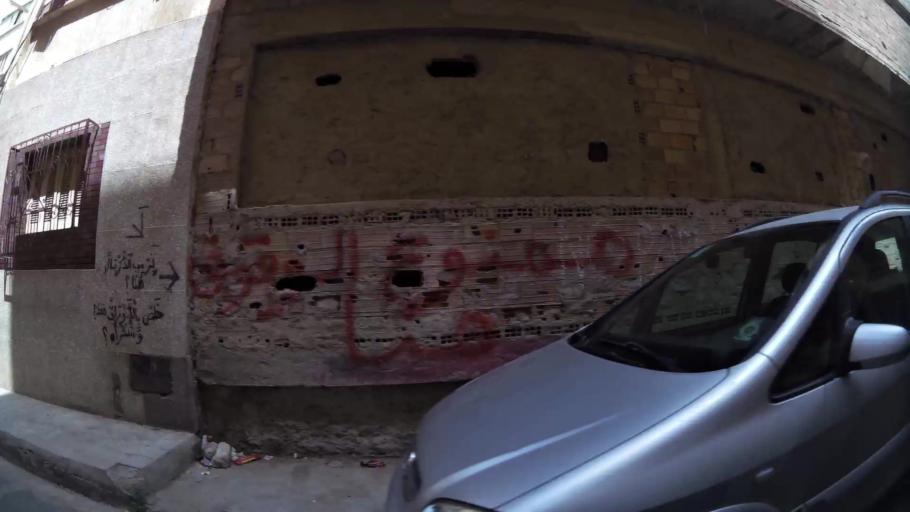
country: MA
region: Oriental
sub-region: Nador
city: Nador
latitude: 35.1715
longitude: -2.9276
